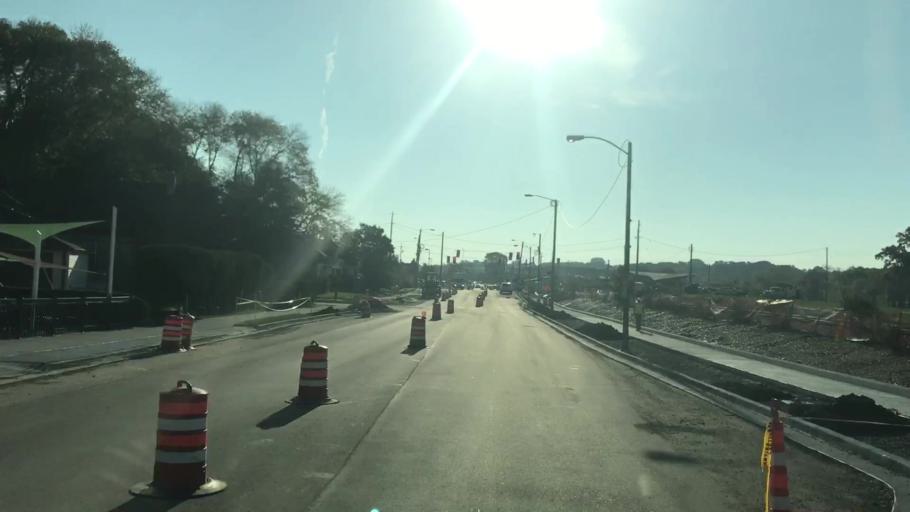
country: US
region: Wisconsin
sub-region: Milwaukee County
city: Wauwatosa
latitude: 43.0478
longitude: -88.0018
